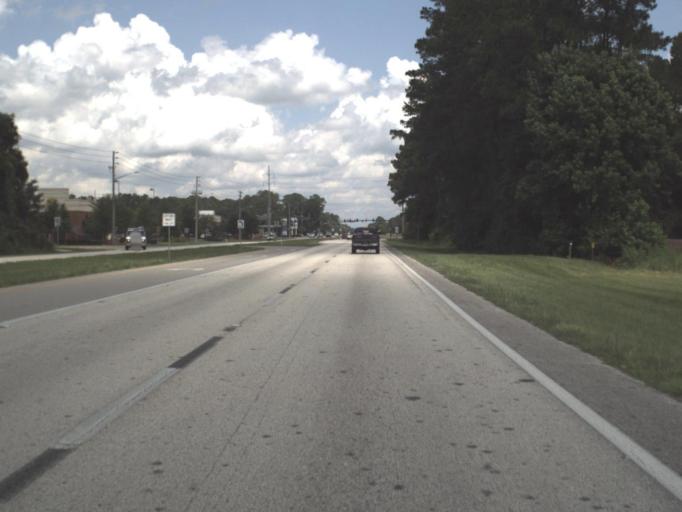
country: US
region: Florida
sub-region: Alachua County
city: Gainesville
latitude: 29.7010
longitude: -82.3409
